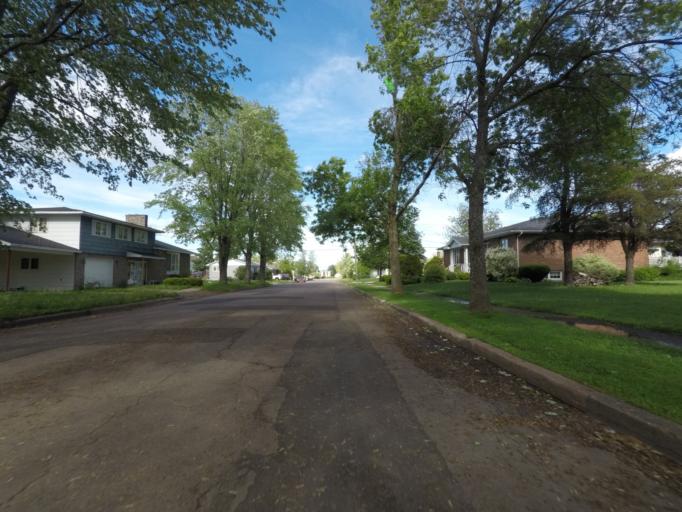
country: CA
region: New Brunswick
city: Moncton
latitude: 46.1031
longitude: -64.8206
